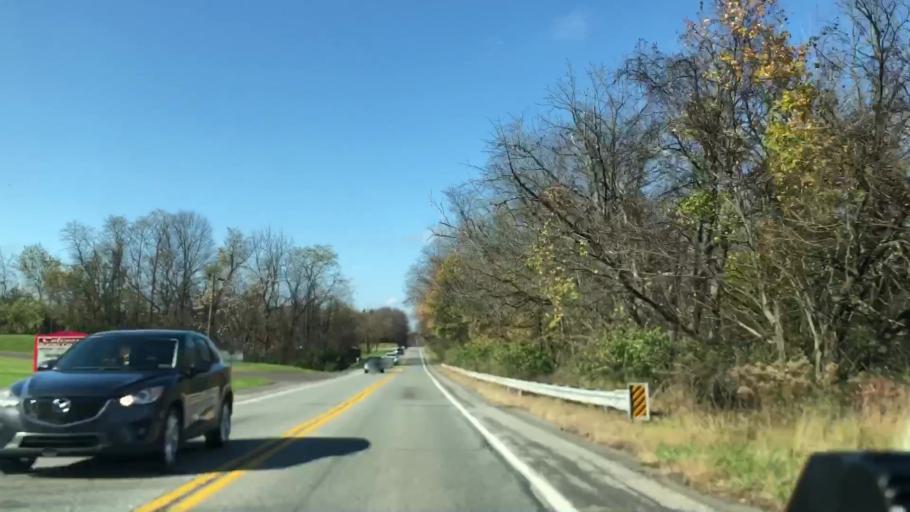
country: US
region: Pennsylvania
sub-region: Montgomery County
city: Sanatoga
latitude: 40.2165
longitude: -75.6055
